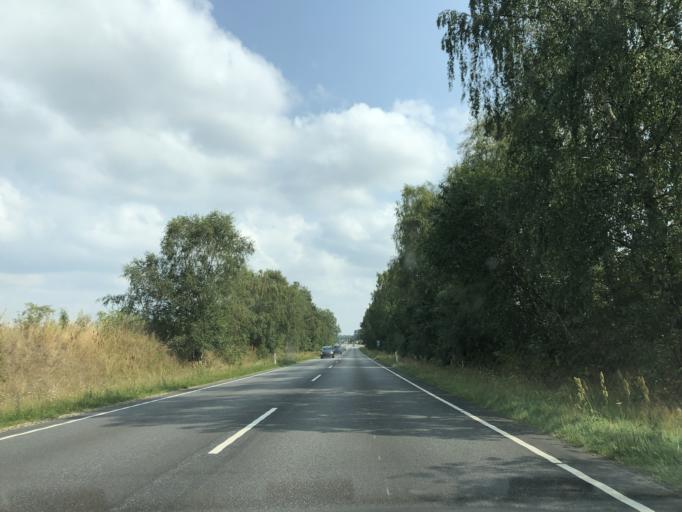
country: DK
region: Central Jutland
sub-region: Viborg Kommune
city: Bjerringbro
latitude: 56.3175
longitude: 9.5760
